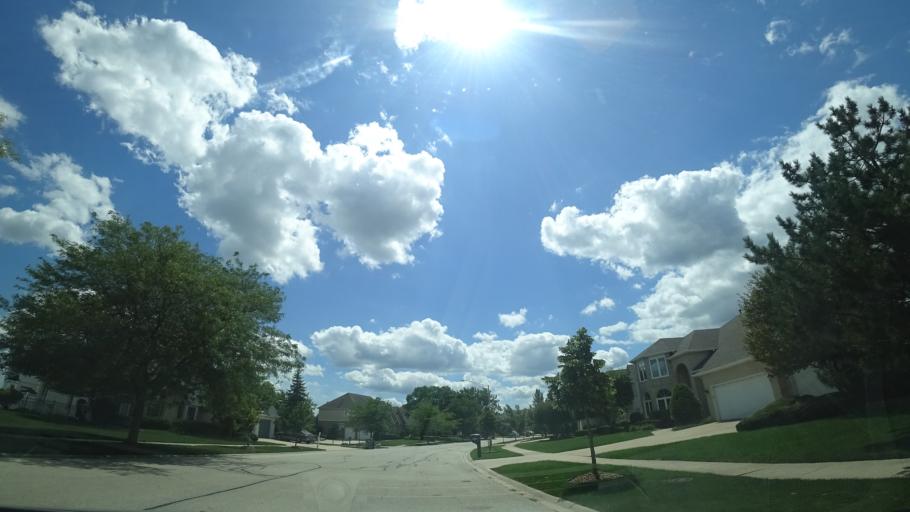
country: US
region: Illinois
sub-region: Will County
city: Homer Glen
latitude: 41.5846
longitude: -87.8936
